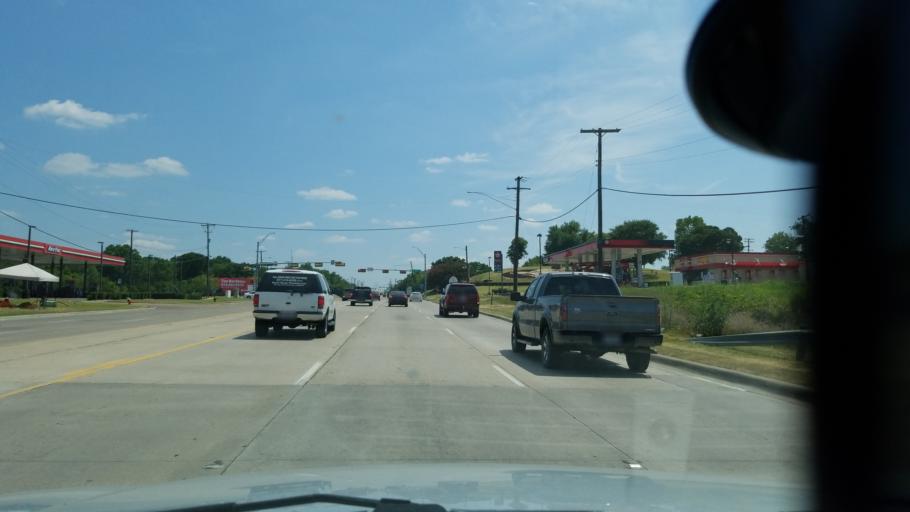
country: US
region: Texas
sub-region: Dallas County
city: Grand Prairie
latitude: 32.7563
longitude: -96.9951
